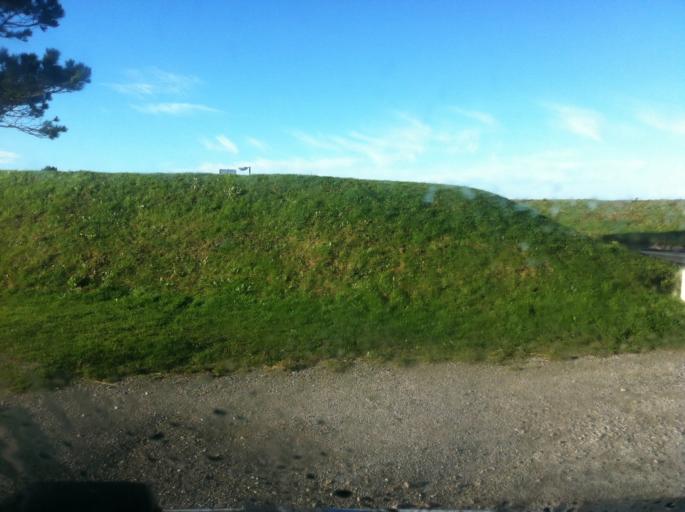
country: FR
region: Haute-Normandie
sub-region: Departement de la Seine-Maritime
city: Le Treport
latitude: 50.0580
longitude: 1.3628
